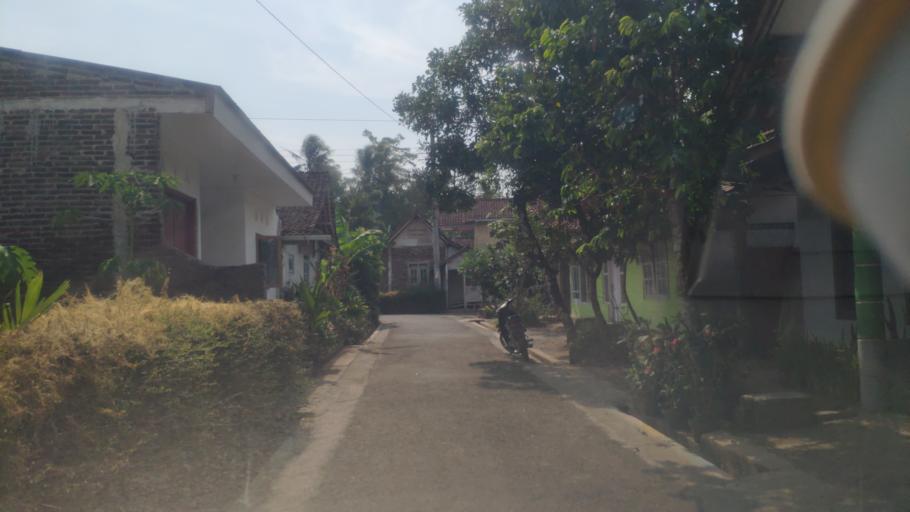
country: ID
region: Central Java
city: Wonosobo
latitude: -7.3892
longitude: 109.7287
